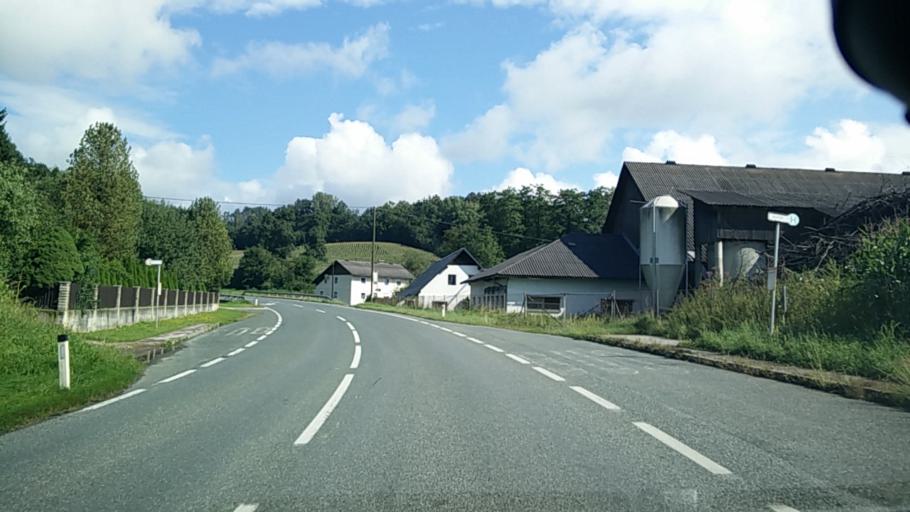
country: AT
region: Carinthia
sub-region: Politischer Bezirk Volkermarkt
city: Gallizien
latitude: 46.6293
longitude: 14.5462
